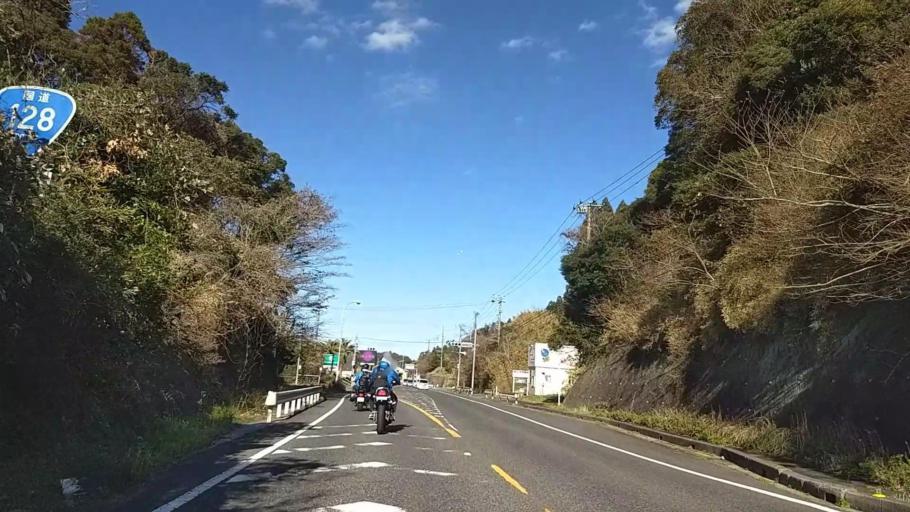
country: JP
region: Chiba
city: Ohara
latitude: 35.2100
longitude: 140.3754
